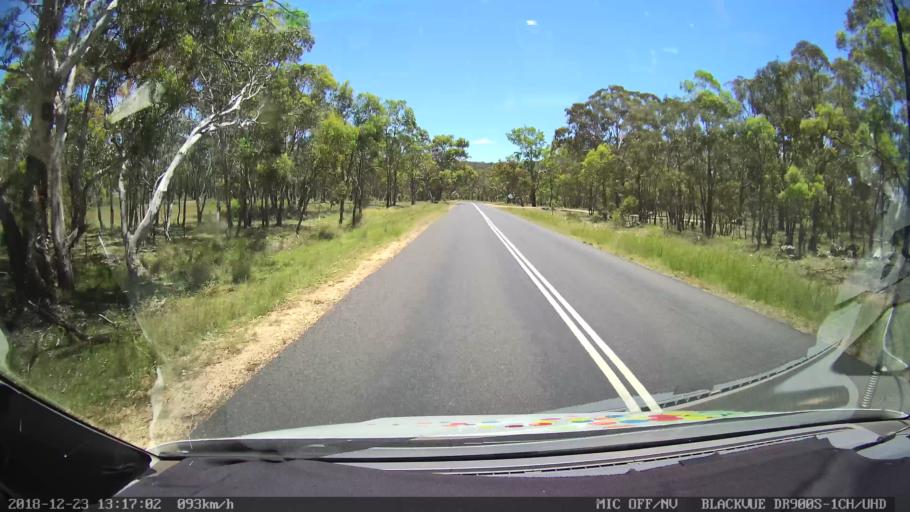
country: AU
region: New South Wales
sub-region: Armidale Dumaresq
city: Armidale
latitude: -30.4947
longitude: 151.4927
